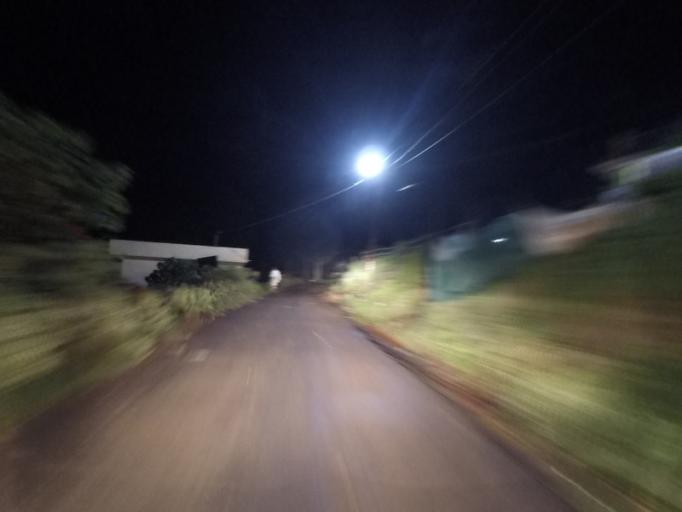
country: IN
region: Tamil Nadu
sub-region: Nilgiri
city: Kotagiri
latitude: 11.4576
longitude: 76.8180
